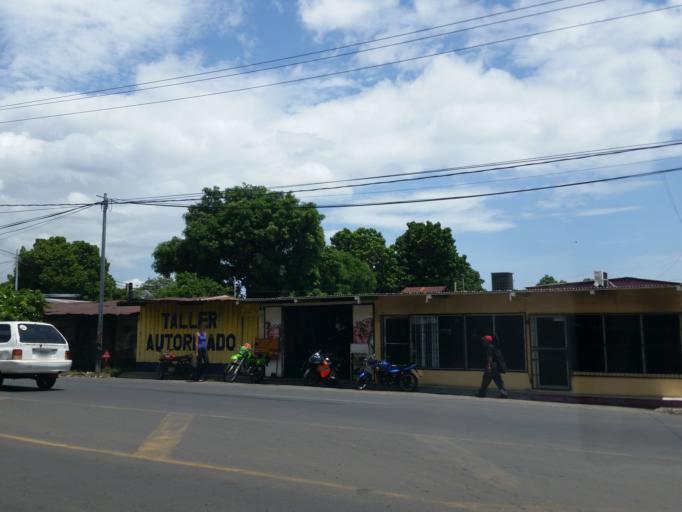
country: NI
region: Managua
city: Managua
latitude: 12.1272
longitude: -86.2448
